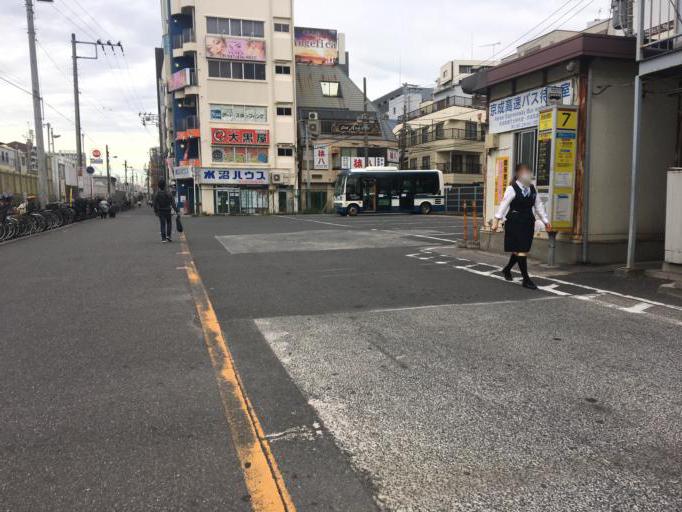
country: JP
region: Chiba
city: Funabashi
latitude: 35.7082
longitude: 139.9586
